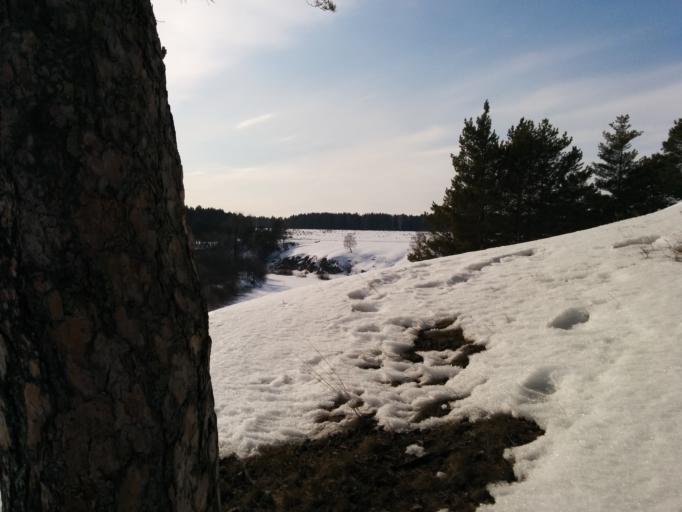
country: RU
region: Bashkortostan
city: Lomovka
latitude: 53.8711
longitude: 58.2554
